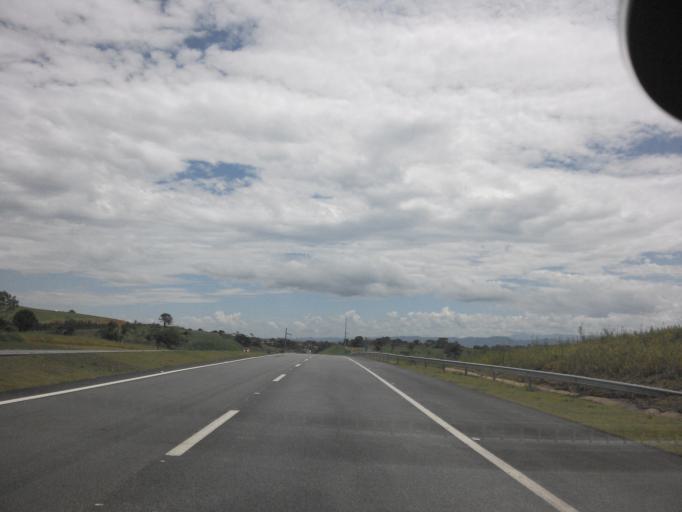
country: BR
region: Sao Paulo
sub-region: Taubate
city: Taubate
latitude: -23.0925
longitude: -45.5756
